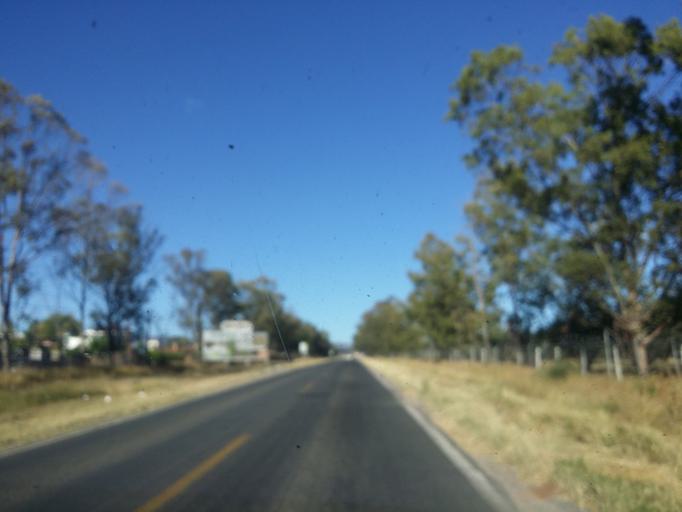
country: MX
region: Guanajuato
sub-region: Silao de la Victoria
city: El Refugio de los Sauces
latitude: 21.0316
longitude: -101.5298
